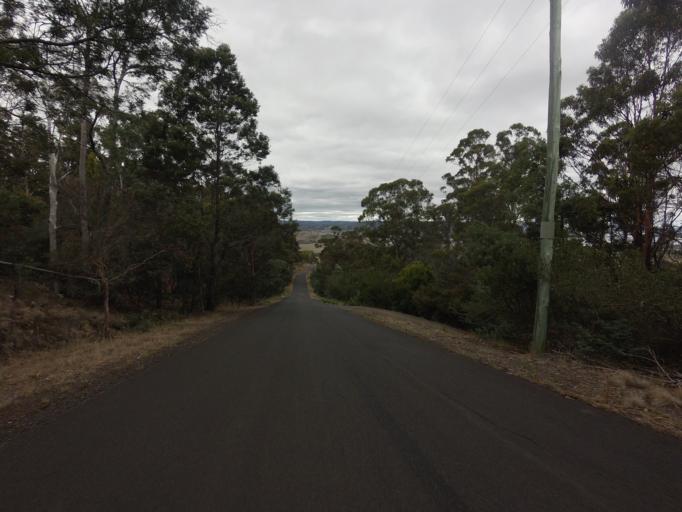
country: AU
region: Tasmania
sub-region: Clarence
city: Cambridge
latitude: -42.7911
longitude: 147.4061
